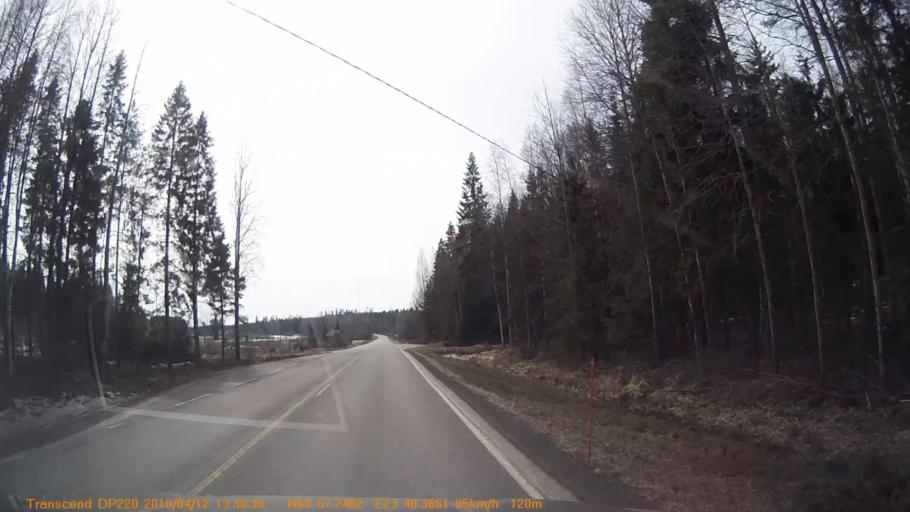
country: FI
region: Haeme
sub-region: Forssa
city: Forssa
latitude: 60.9623
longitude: 23.6725
